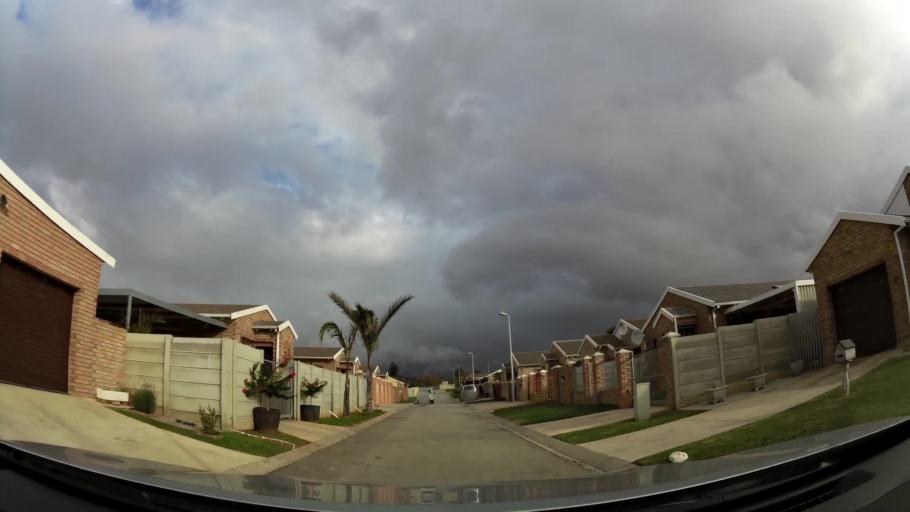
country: ZA
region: Eastern Cape
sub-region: Nelson Mandela Bay Metropolitan Municipality
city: Uitenhage
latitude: -33.7987
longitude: 25.4555
